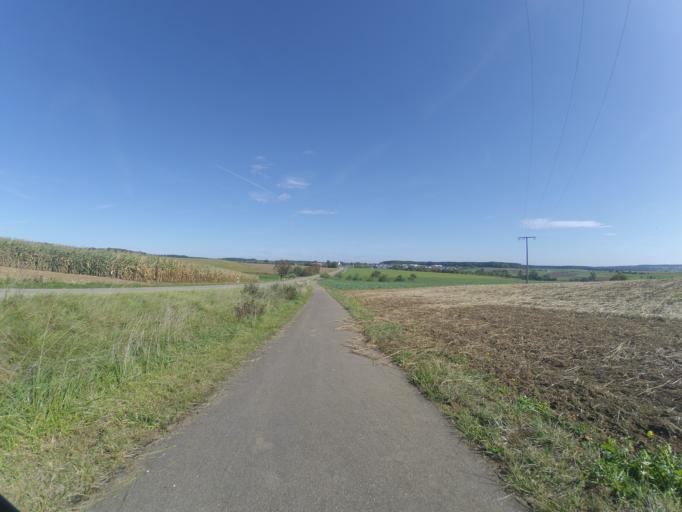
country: DE
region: Baden-Wuerttemberg
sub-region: Tuebingen Region
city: Borslingen
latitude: 48.5466
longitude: 10.0686
